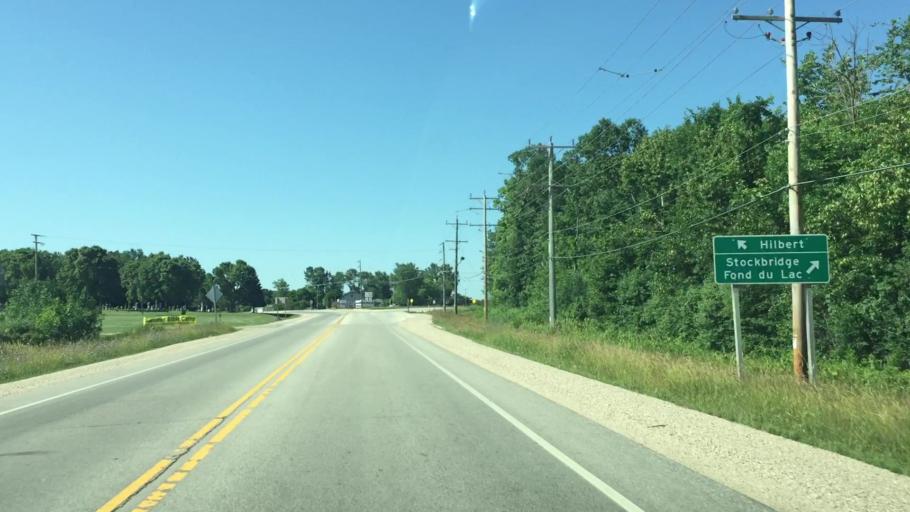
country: US
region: Wisconsin
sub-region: Calumet County
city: Sherwood
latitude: 44.1642
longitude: -88.2641
